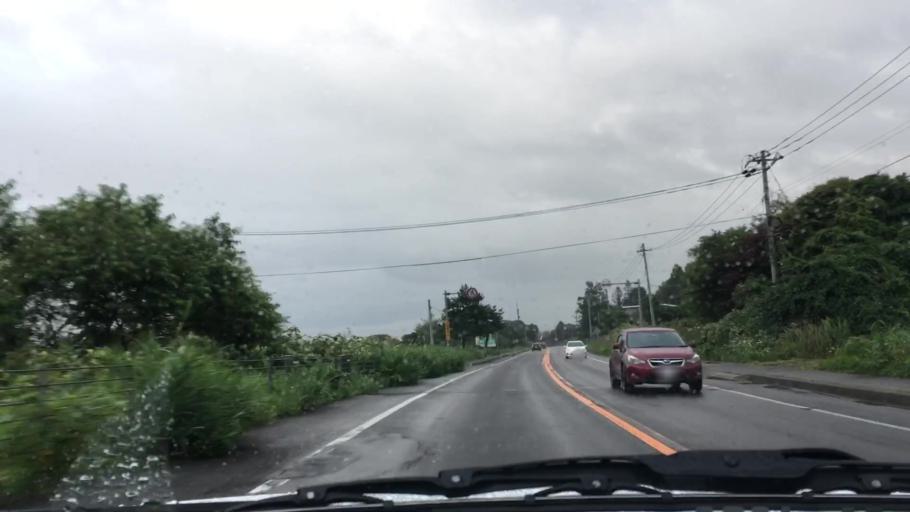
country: JP
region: Hokkaido
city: Nanae
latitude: 42.1782
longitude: 140.4470
